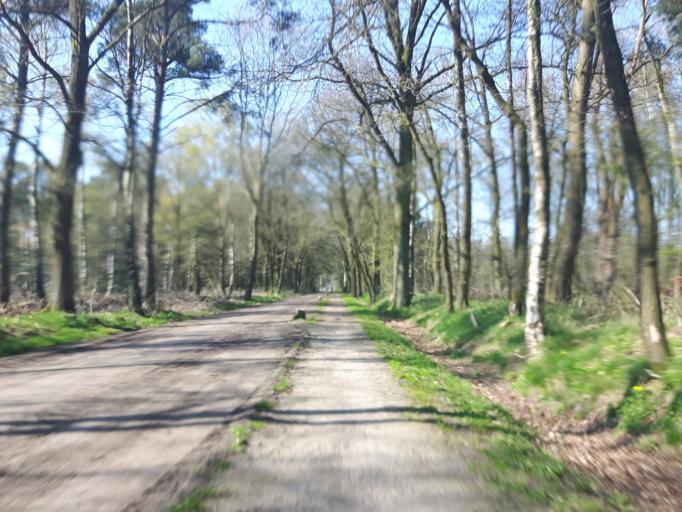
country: NL
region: Overijssel
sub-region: Gemeente Haaksbergen
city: Haaksbergen
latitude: 52.1828
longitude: 6.8165
